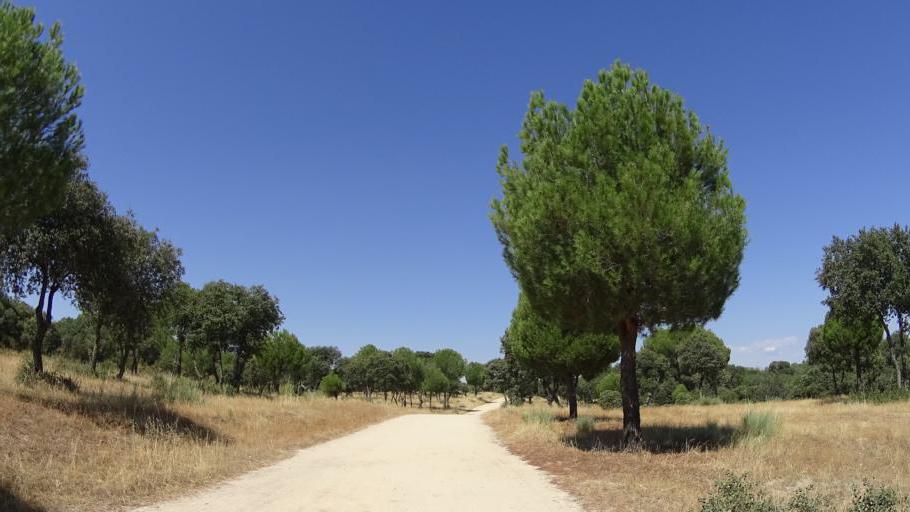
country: ES
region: Madrid
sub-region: Provincia de Madrid
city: Boadilla del Monte
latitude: 40.4341
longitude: -3.8575
